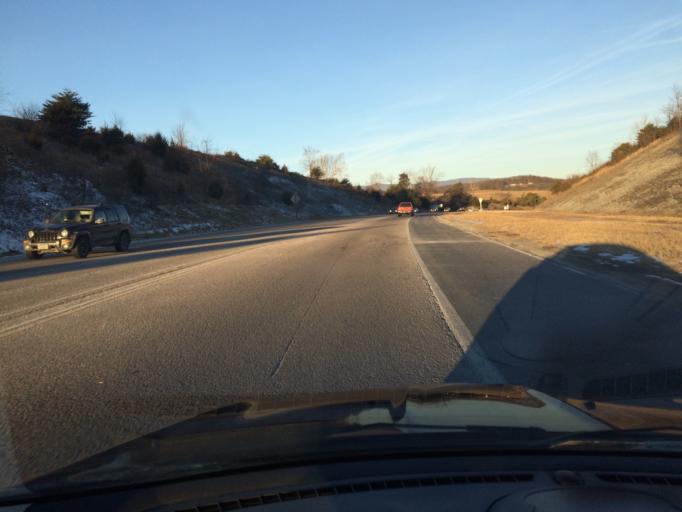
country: US
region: Virginia
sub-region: Augusta County
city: Jolivue
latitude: 38.1262
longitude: -79.0847
